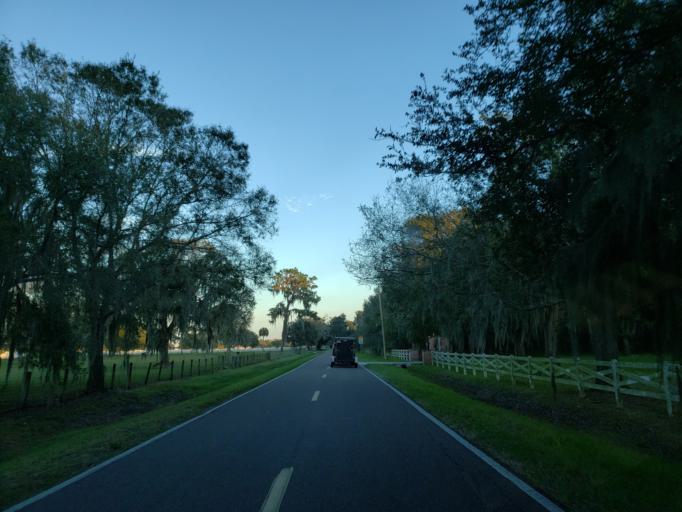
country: US
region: Florida
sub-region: Hillsborough County
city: Fish Hawk
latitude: 27.8287
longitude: -82.1864
